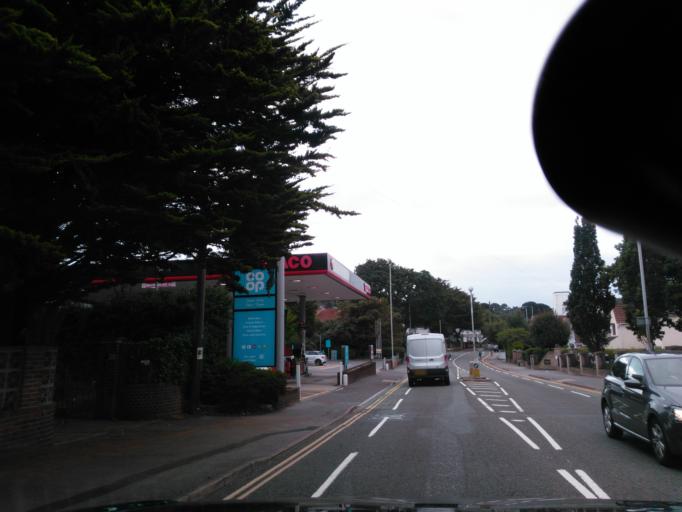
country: GB
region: England
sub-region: Dorset
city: Parkstone
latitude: 50.7101
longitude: -1.9467
